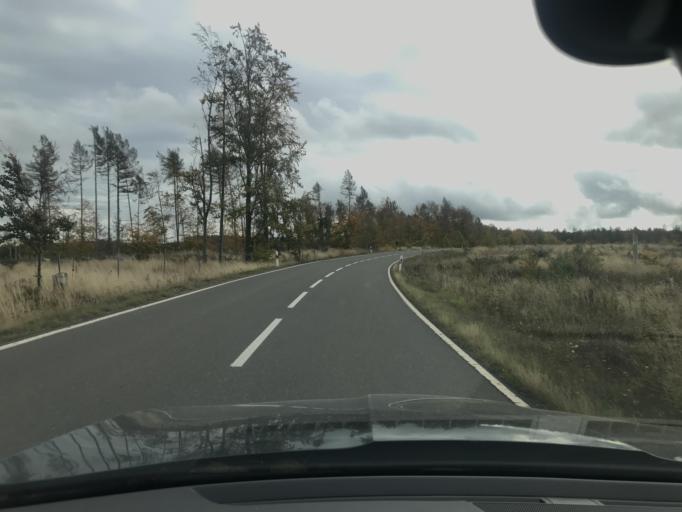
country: DE
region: Saxony-Anhalt
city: Friedrichsbrunn
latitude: 51.7078
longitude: 11.0190
